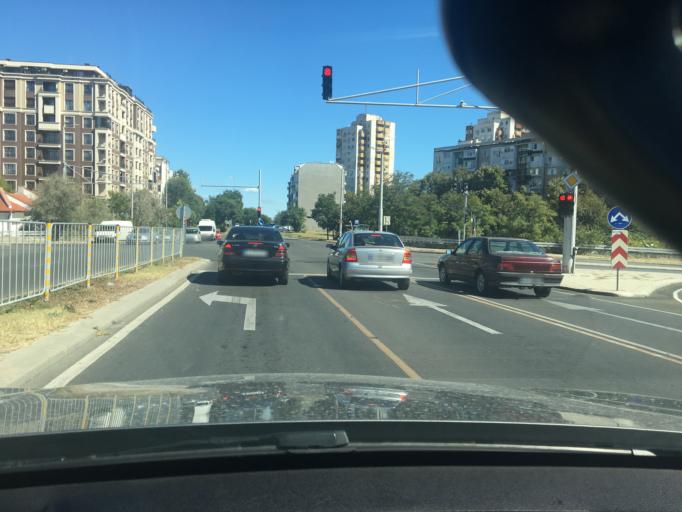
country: BG
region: Burgas
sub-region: Obshtina Burgas
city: Burgas
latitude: 42.5209
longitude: 27.4651
